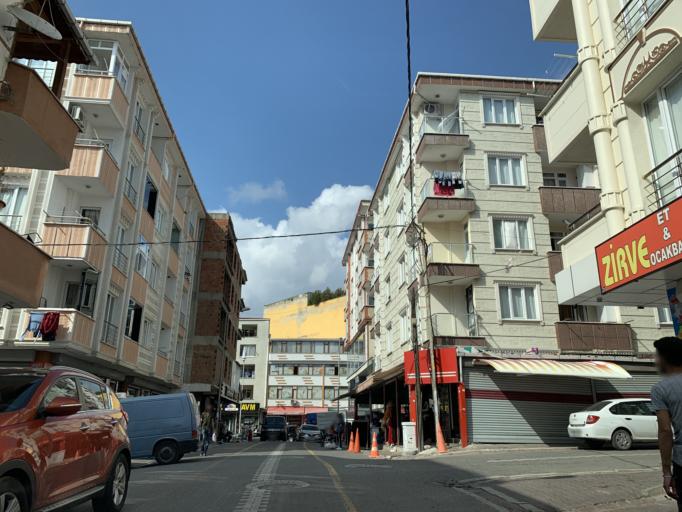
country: TR
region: Istanbul
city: Esenyurt
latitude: 41.0353
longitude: 28.6738
